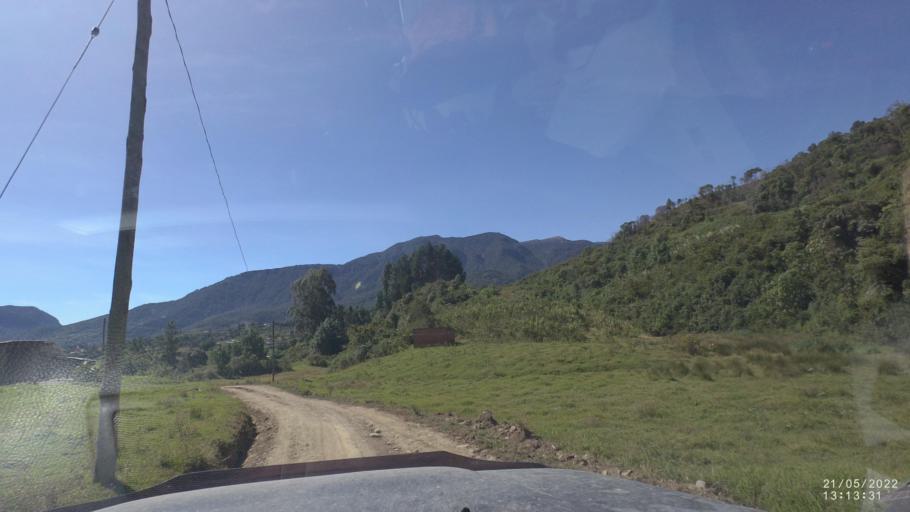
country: BO
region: Cochabamba
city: Colomi
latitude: -17.1379
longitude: -65.9407
